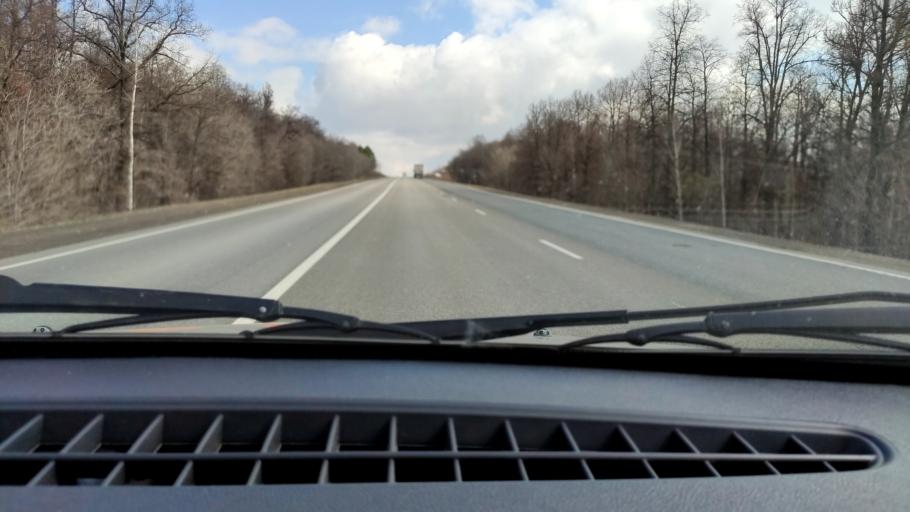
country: RU
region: Bashkortostan
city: Iglino
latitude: 54.7939
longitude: 56.5773
